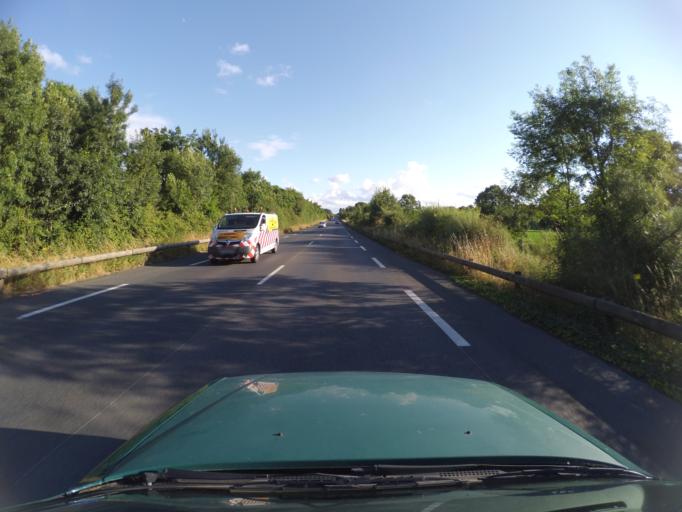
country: FR
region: Pays de la Loire
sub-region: Departement de la Vendee
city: Saint-Hilaire-de-Loulay
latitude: 46.9970
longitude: -1.3481
